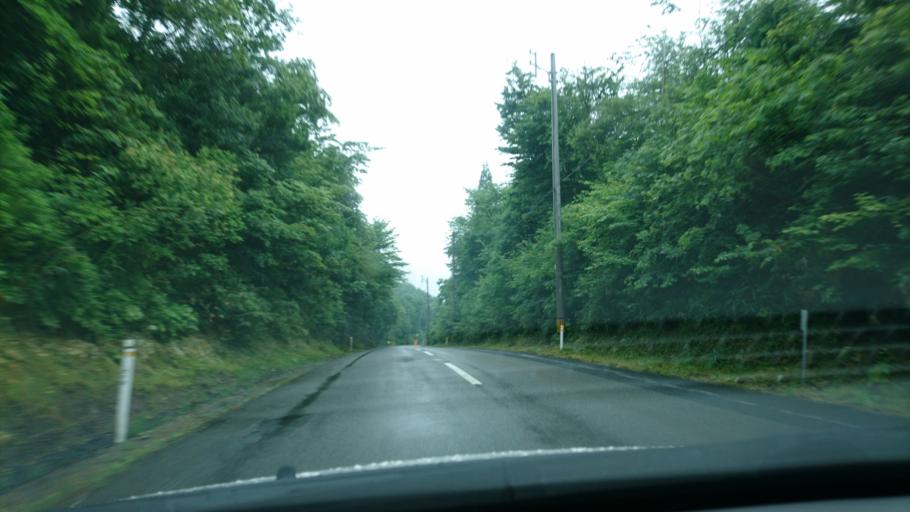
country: JP
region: Iwate
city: Ichinoseki
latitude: 38.9175
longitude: 141.0269
